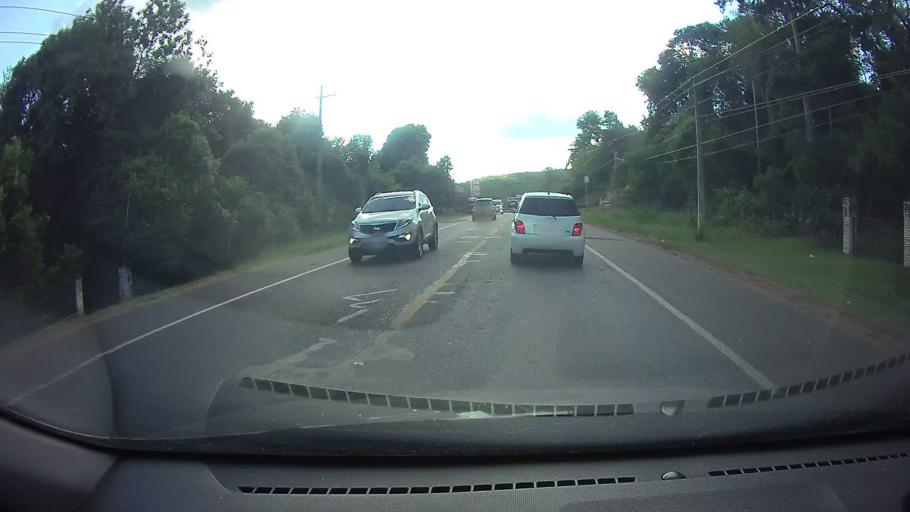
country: PY
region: Cordillera
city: Caacupe
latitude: -25.3903
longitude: -57.0779
